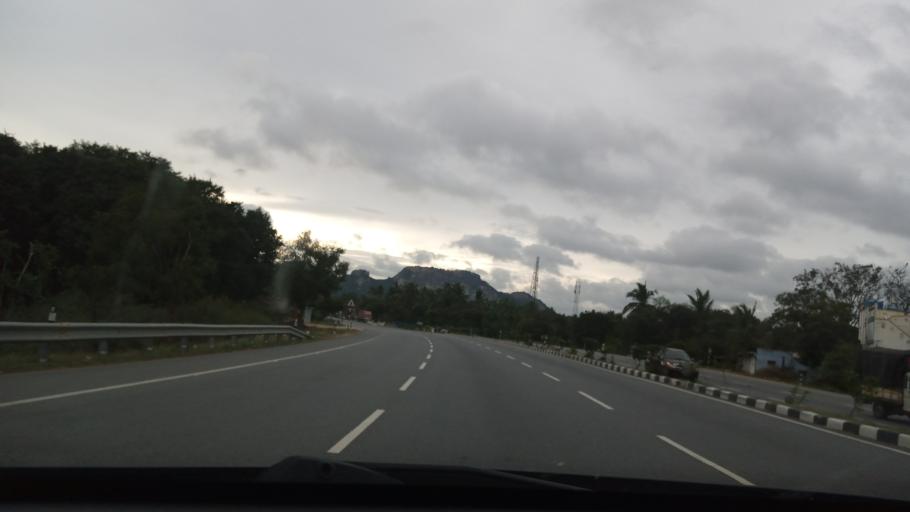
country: IN
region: Tamil Nadu
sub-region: Vellore
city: Jolarpettai
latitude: 12.5384
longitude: 78.4054
